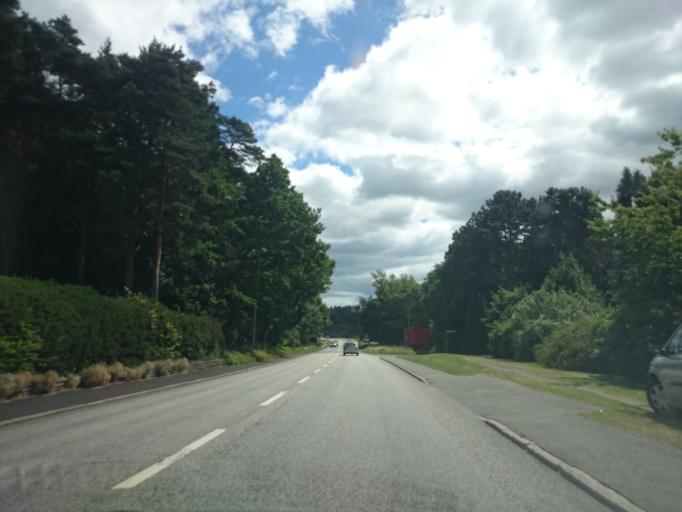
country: SE
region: Skane
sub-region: Kristianstads Kommun
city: Degeberga
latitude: 55.8281
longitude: 14.0934
